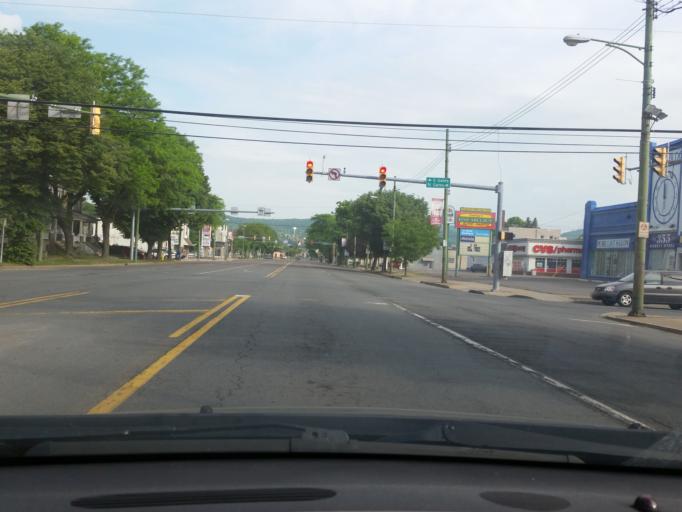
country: US
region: Pennsylvania
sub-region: Luzerne County
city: Kingston
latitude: 41.2557
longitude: -75.8914
